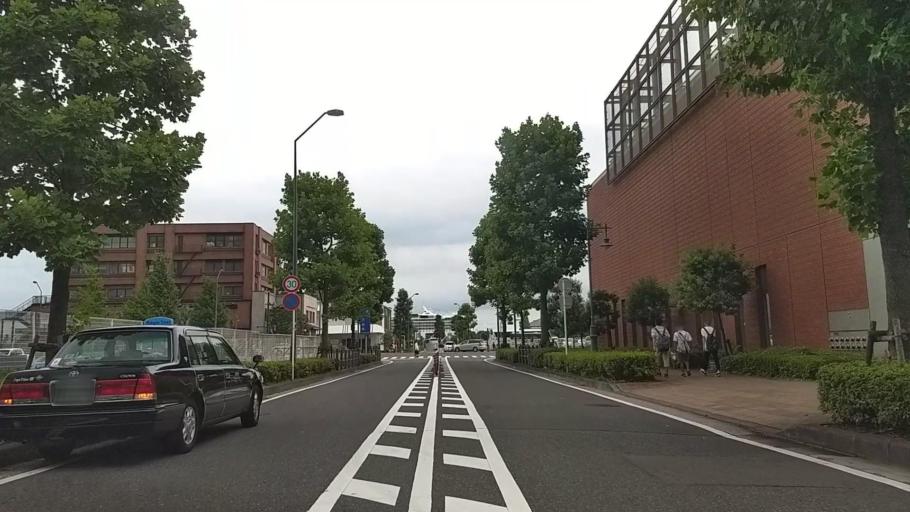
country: JP
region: Kanagawa
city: Yokohama
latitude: 35.4552
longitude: 139.6403
